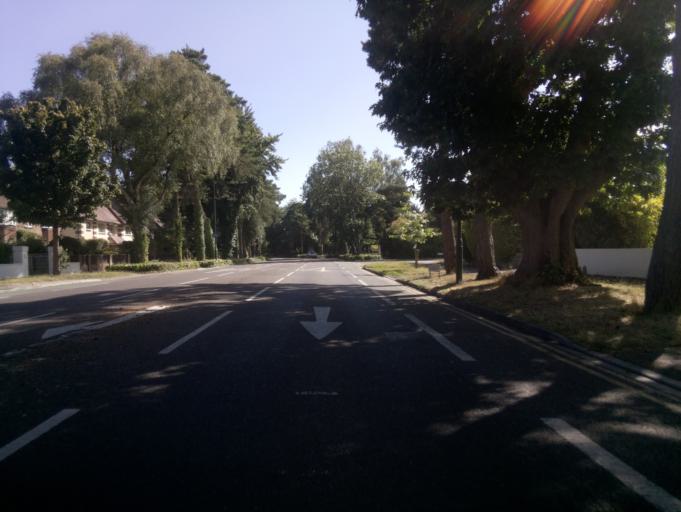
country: GB
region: England
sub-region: Bournemouth
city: Bournemouth
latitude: 50.7348
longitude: -1.8932
